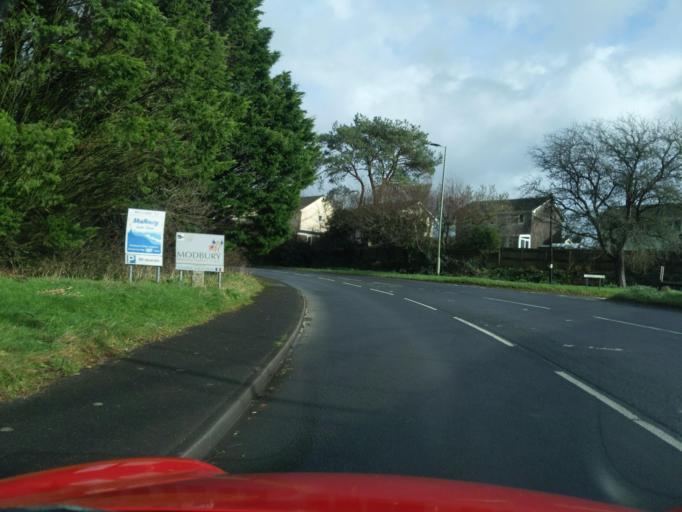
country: GB
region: England
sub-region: Devon
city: Modbury
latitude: 50.3496
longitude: -3.8930
